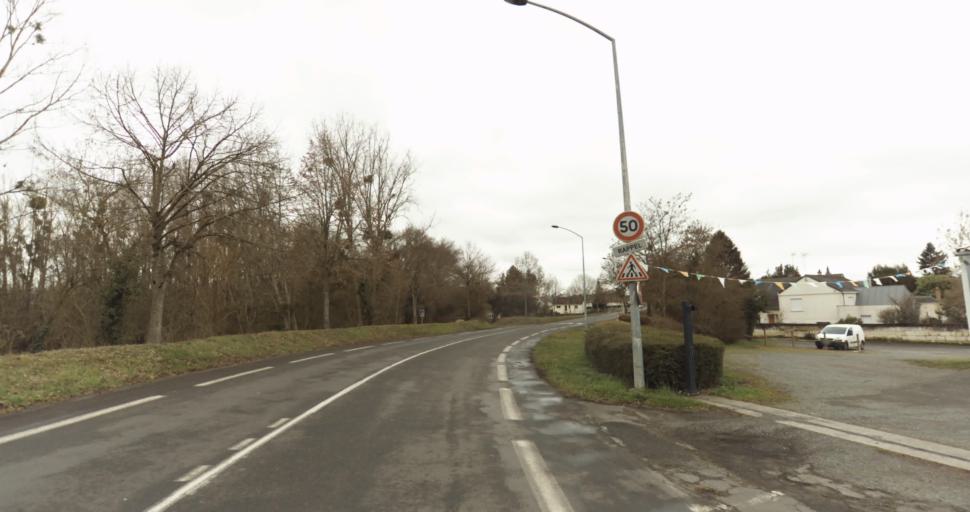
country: FR
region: Pays de la Loire
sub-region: Departement de Maine-et-Loire
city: Saumur
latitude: 47.2490
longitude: -0.0863
